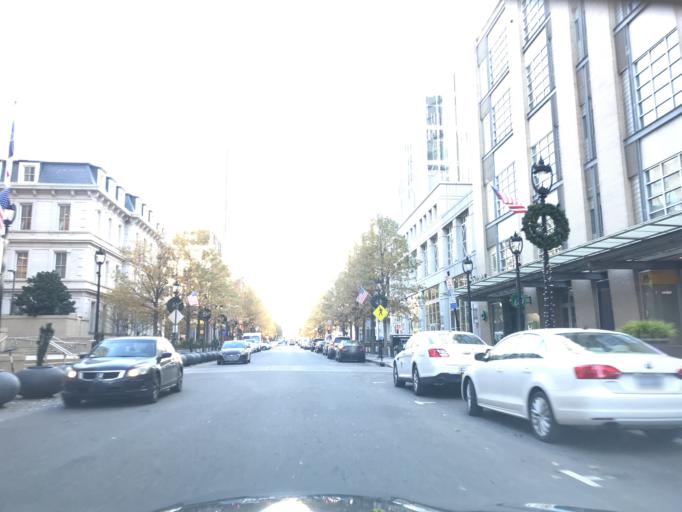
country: US
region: North Carolina
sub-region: Wake County
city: Raleigh
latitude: 35.7759
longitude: -78.6393
